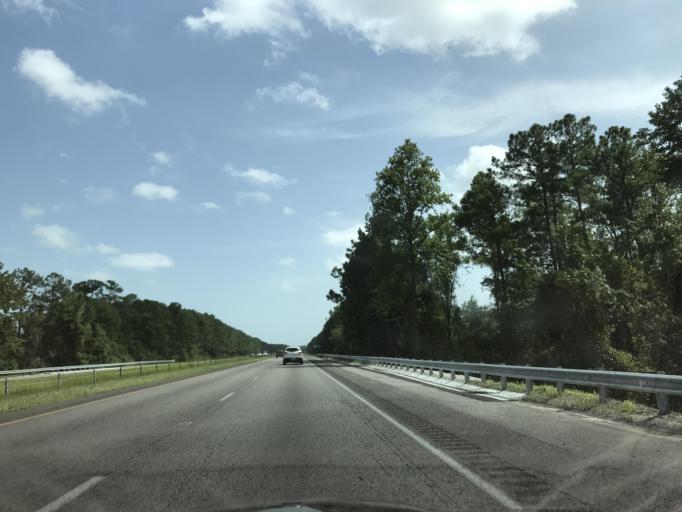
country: US
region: North Carolina
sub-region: New Hanover County
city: Skippers Corner
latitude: 34.3395
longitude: -77.8788
